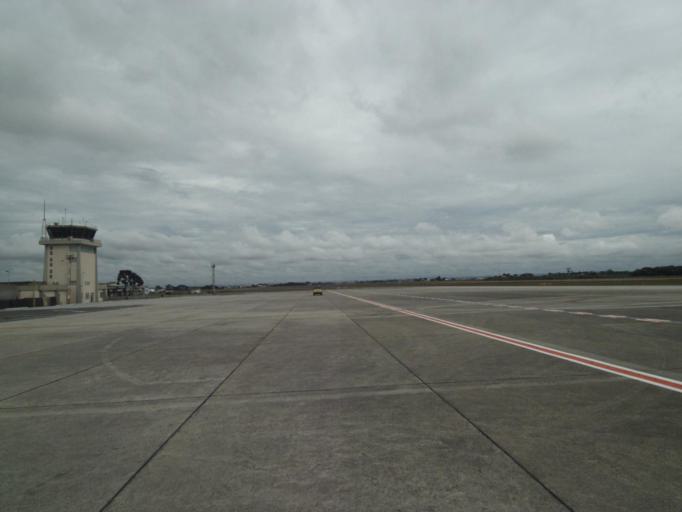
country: BR
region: Parana
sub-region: Sao Jose Dos Pinhais
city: Sao Jose dos Pinhais
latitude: -25.5320
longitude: -49.1747
